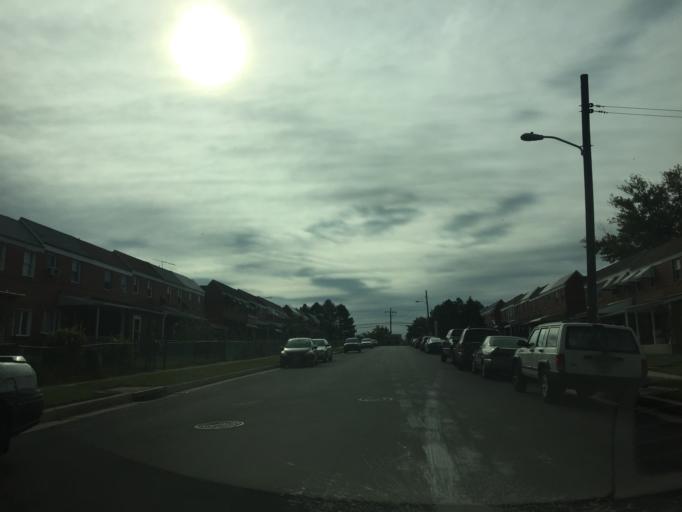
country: US
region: Maryland
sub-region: Baltimore County
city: Dundalk
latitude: 39.2819
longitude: -76.5066
